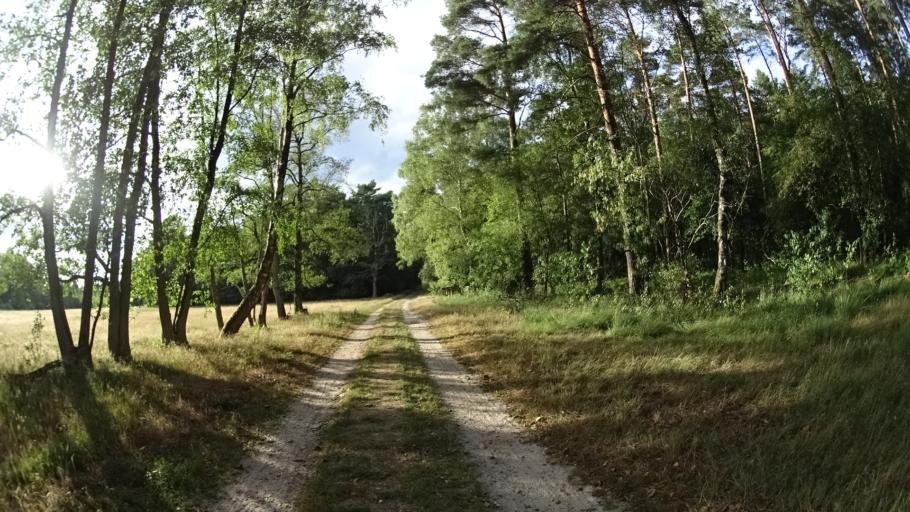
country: DE
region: Lower Saxony
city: Handeloh
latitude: 53.2231
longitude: 9.8765
